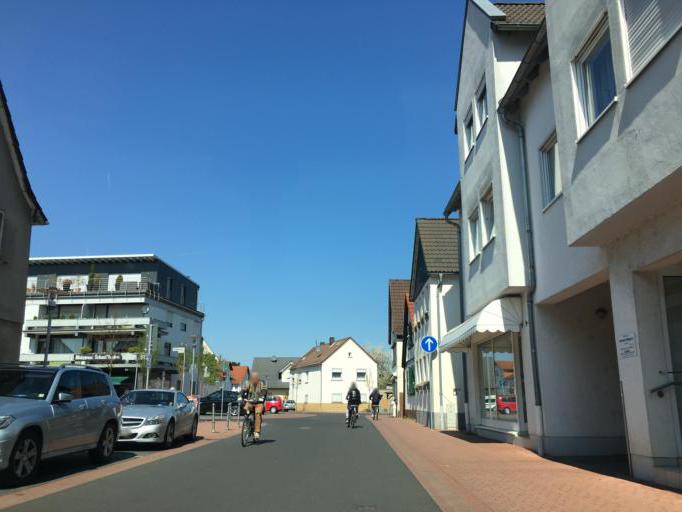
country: DE
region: Hesse
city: Obertshausen
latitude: 50.0836
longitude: 8.8668
